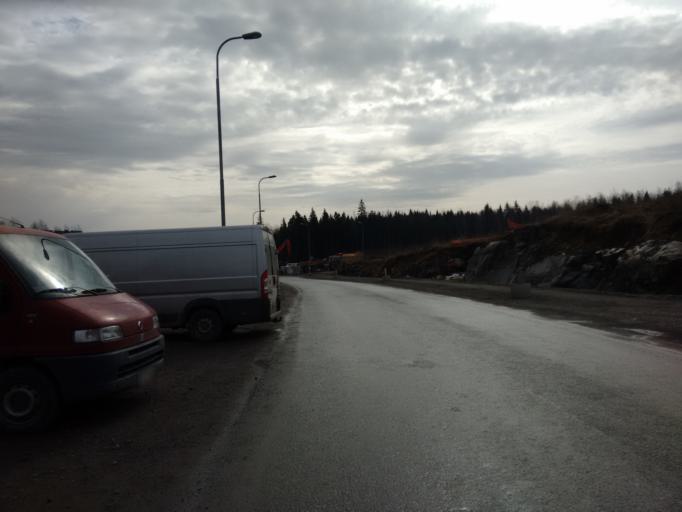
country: FI
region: Pirkanmaa
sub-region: Tampere
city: Tampere
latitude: 61.4319
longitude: 23.8039
